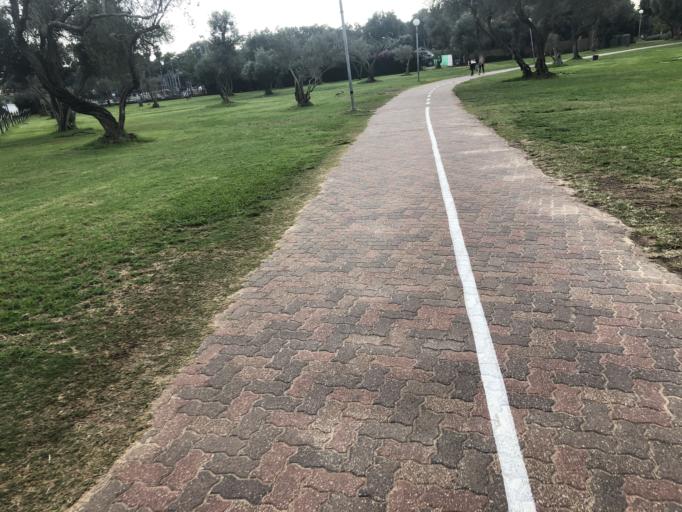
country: IL
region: Tel Aviv
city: Giv`atayim
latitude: 32.0479
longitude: 34.8254
